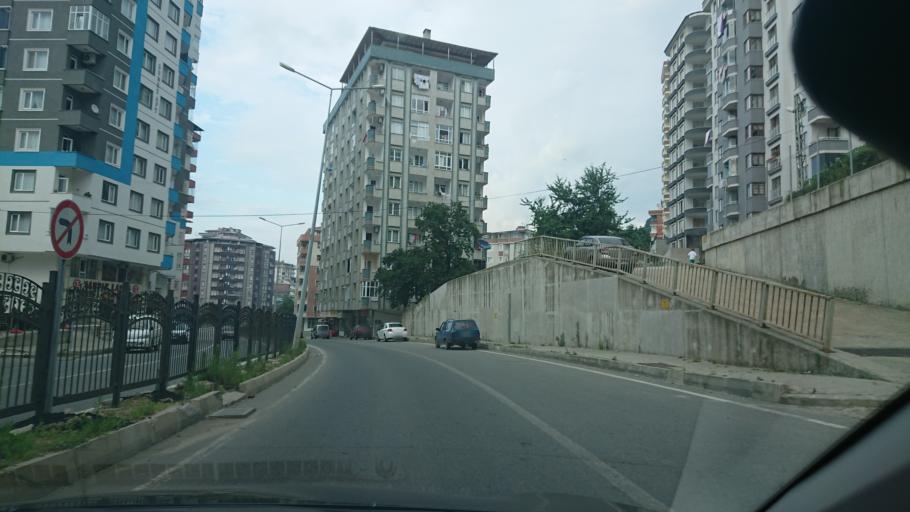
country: TR
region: Rize
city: Rize
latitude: 41.0210
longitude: 40.5327
